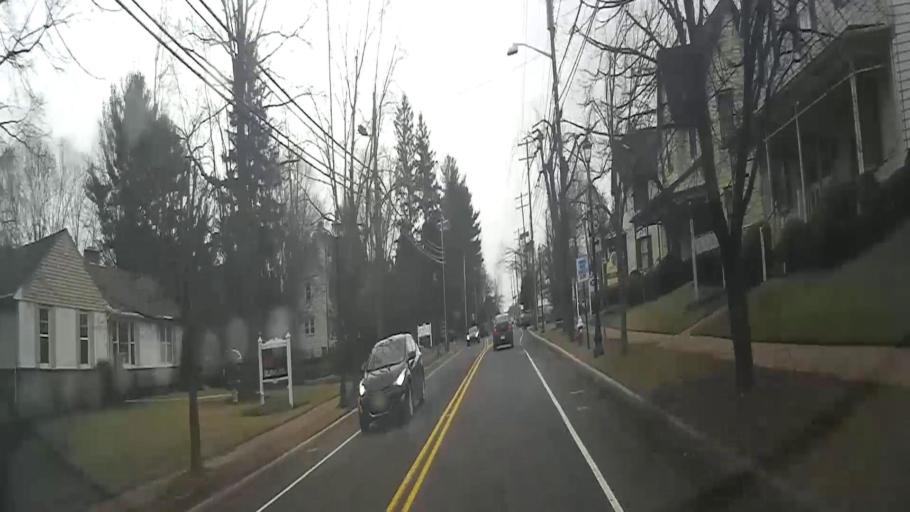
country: US
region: New Jersey
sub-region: Burlington County
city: Marlton
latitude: 39.8879
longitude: -74.9221
